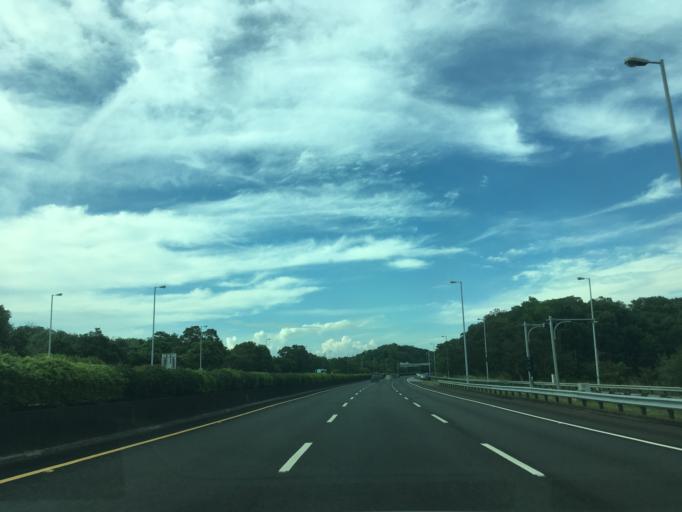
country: TW
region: Taiwan
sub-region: Chiayi
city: Jiayi Shi
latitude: 23.5220
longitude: 120.4849
